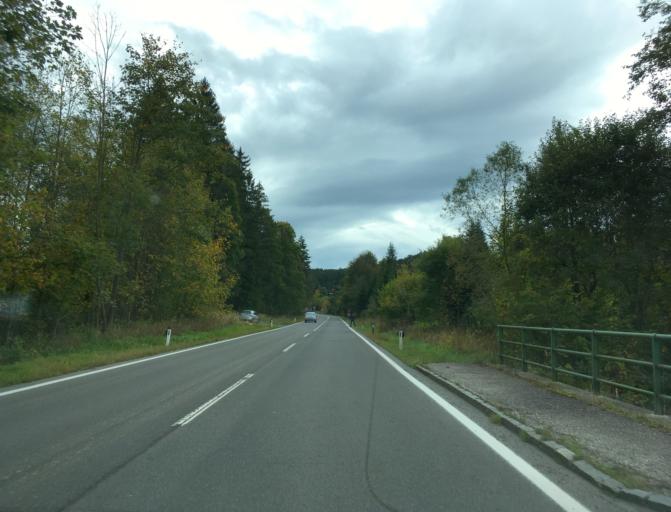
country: AT
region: Lower Austria
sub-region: Politischer Bezirk Neunkirchen
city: Thomasberg
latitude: 47.5501
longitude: 16.1435
